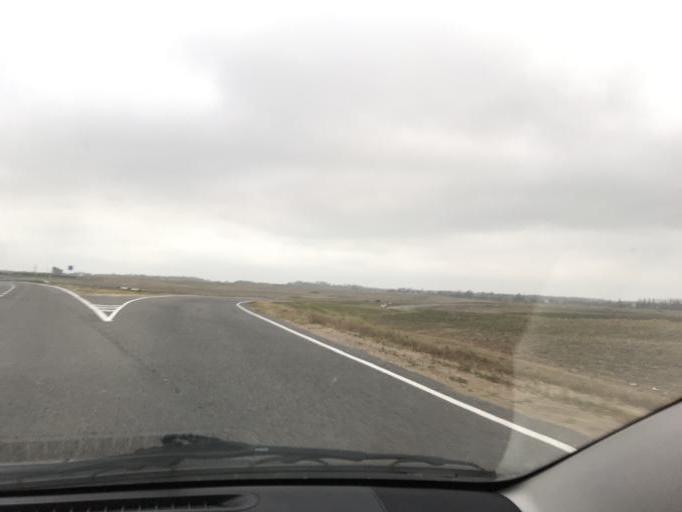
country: BY
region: Vitebsk
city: Vitebsk
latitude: 55.1581
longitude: 30.0653
